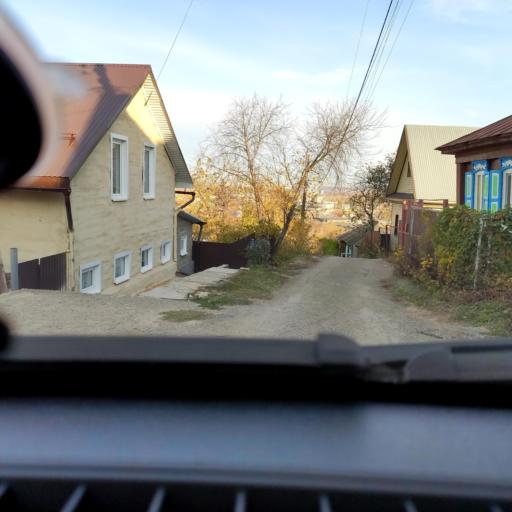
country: RU
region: Bashkortostan
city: Ufa
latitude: 54.7369
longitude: 55.9272
